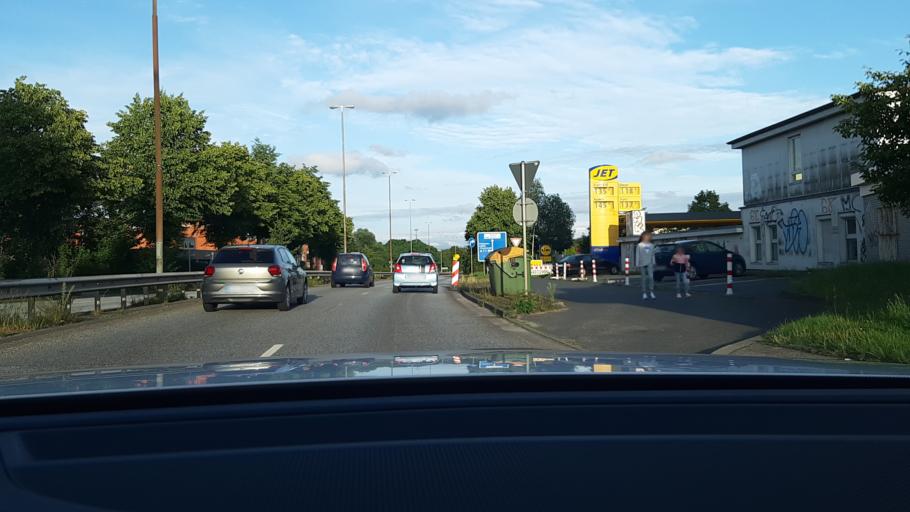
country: DE
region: Schleswig-Holstein
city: Stockelsdorf
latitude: 53.8822
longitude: 10.6576
